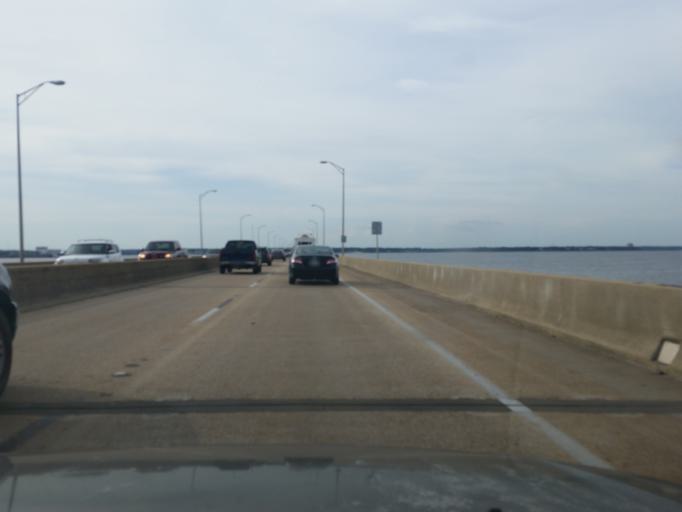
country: US
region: Florida
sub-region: Santa Rosa County
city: Gulf Breeze
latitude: 30.3831
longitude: -87.1808
